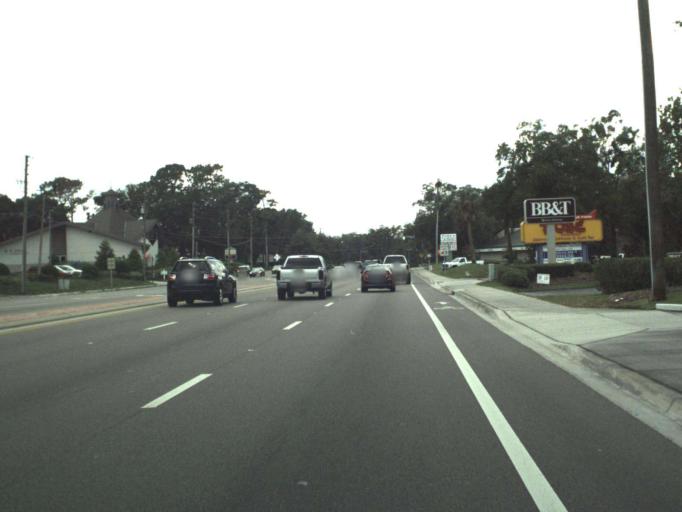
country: US
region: Florida
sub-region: Seminole County
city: Wekiwa Springs
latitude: 28.6886
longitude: -81.3926
